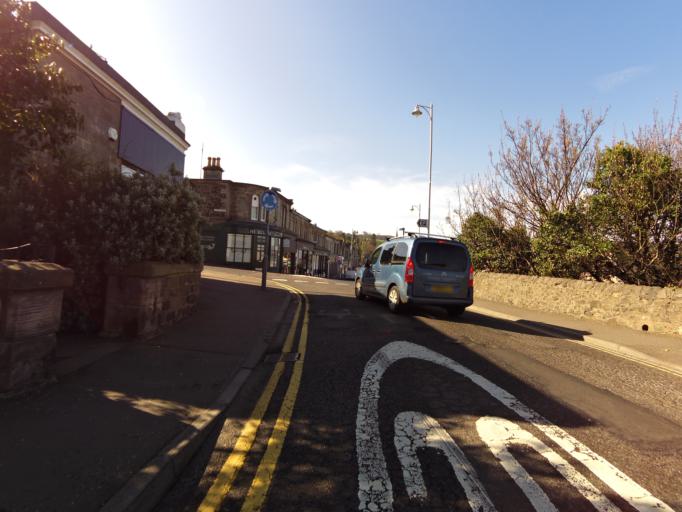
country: GB
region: Scotland
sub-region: Fife
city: Newport-On-Tay
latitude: 56.4404
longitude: -2.9414
